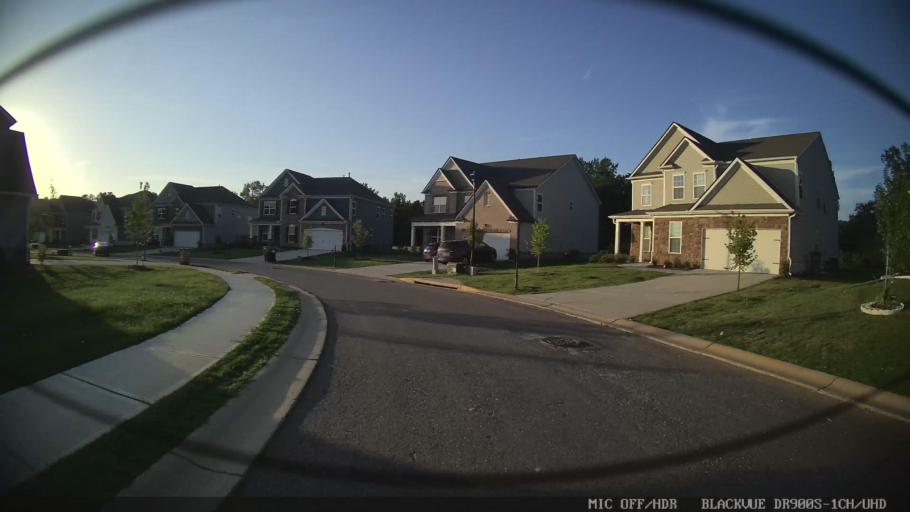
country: US
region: Georgia
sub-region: Forsyth County
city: Cumming
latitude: 34.2194
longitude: -84.2065
